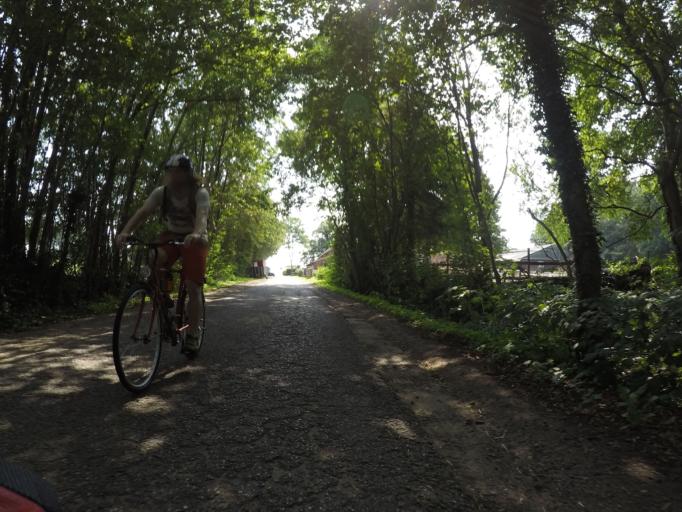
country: DE
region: Schleswig-Holstein
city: Kisdorf
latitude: 53.7951
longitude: 10.0308
